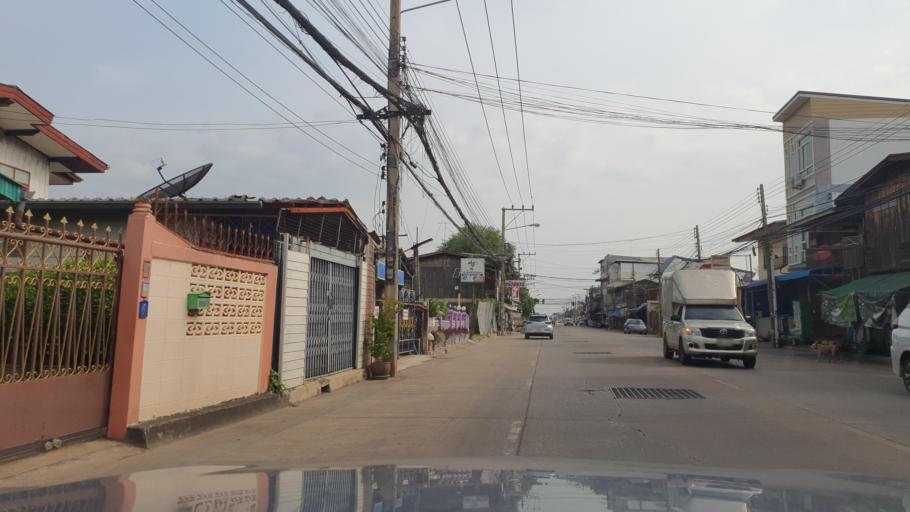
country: TH
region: Phitsanulok
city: Phitsanulok
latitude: 16.8369
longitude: 100.2656
